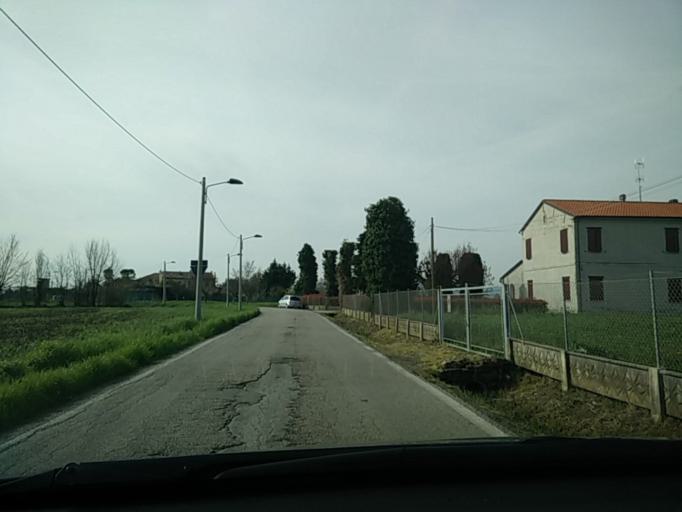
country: IT
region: Emilia-Romagna
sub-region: Provincia di Rimini
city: Santa Giustina
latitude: 44.0799
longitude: 12.5055
